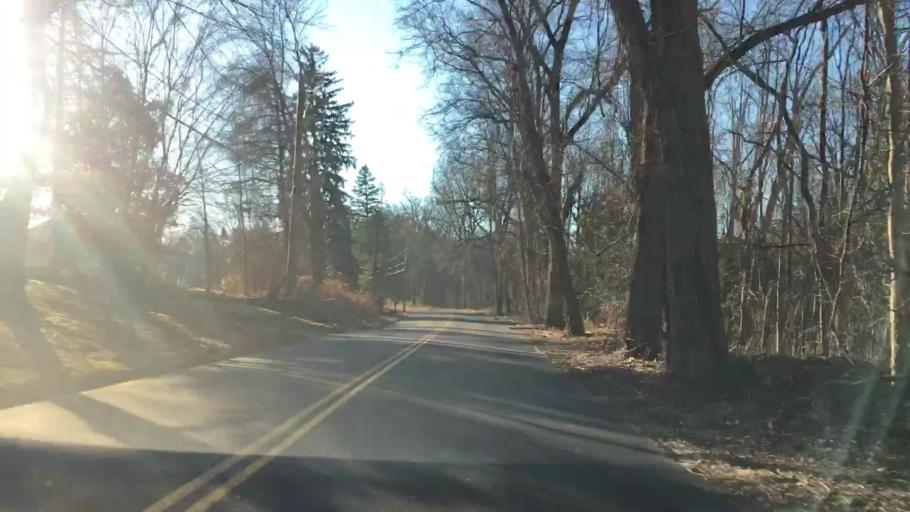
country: US
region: Connecticut
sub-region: New Haven County
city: Cheshire Village
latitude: 41.5545
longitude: -72.8696
